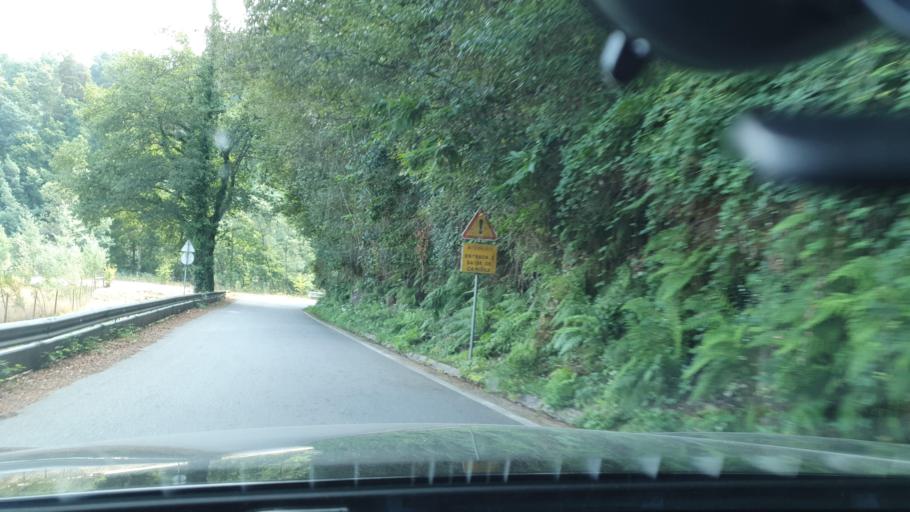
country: PT
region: Braga
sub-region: Vieira do Minho
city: Vieira do Minho
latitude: 41.6865
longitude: -8.0926
